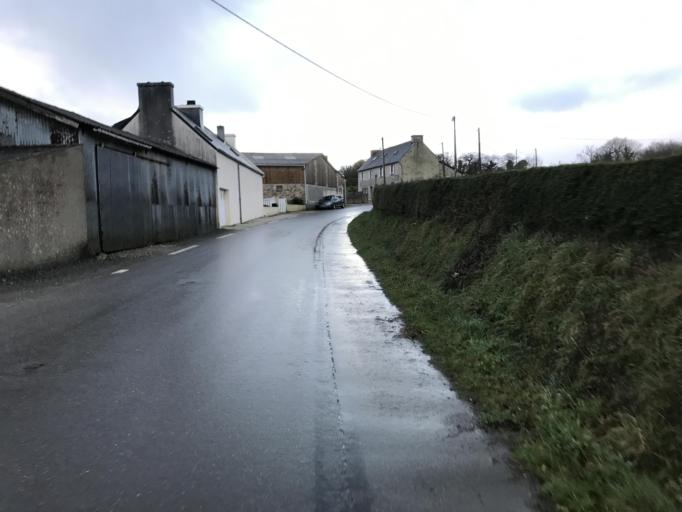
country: FR
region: Brittany
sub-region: Departement du Finistere
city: Plougastel-Daoulas
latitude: 48.3588
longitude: -4.3446
